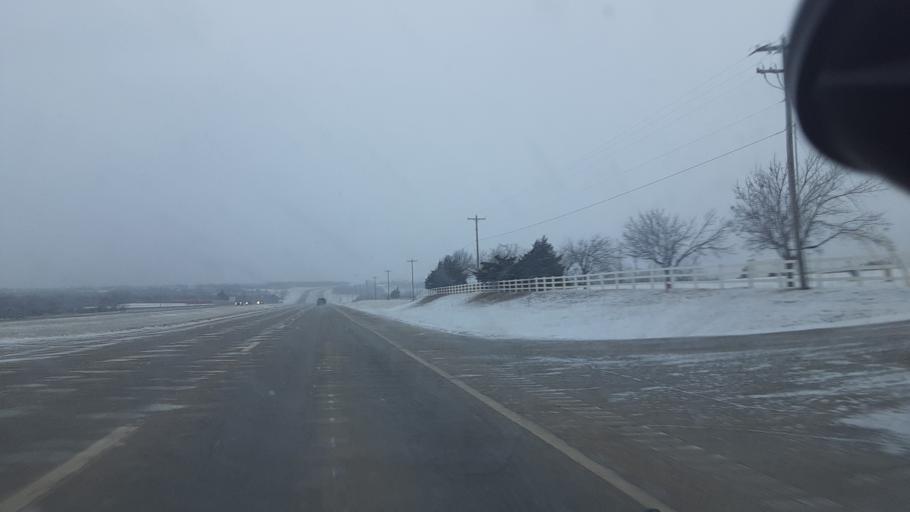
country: US
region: Oklahoma
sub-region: Logan County
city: Guthrie
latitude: 35.8953
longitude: -97.3595
